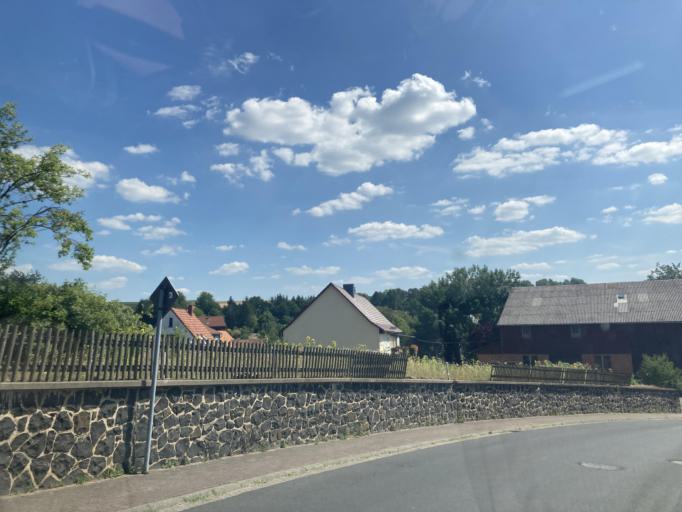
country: DE
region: Hesse
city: Grebenau
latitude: 50.7223
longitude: 9.4203
